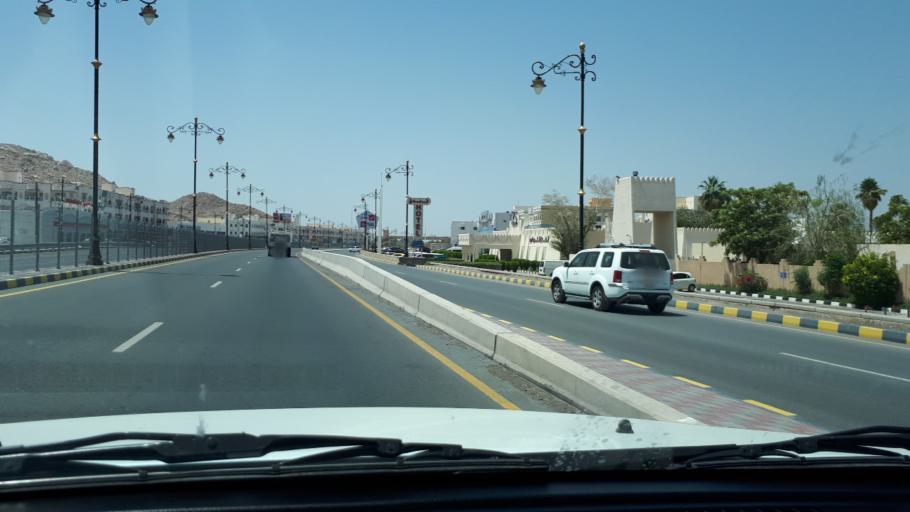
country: OM
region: Muhafazat ad Dakhiliyah
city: Nizwa
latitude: 22.8962
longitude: 57.5315
